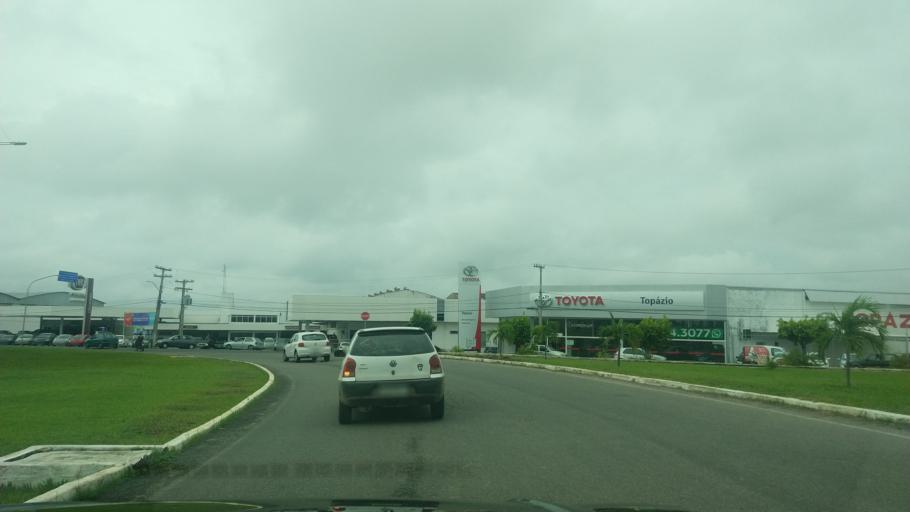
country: BR
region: Bahia
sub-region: Paulo Afonso
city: Paulo Afonso
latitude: -9.4011
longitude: -38.2389
